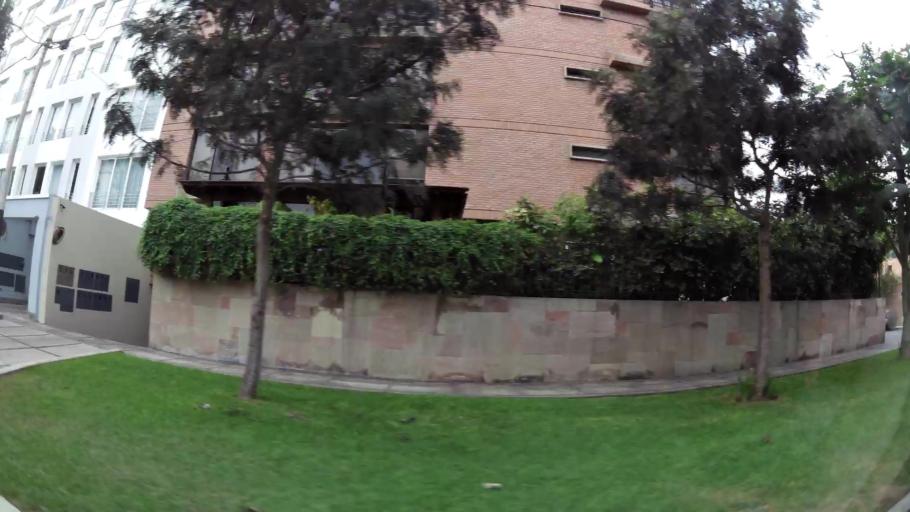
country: PE
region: Lima
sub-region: Lima
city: San Isidro
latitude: -12.1043
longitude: -77.0452
